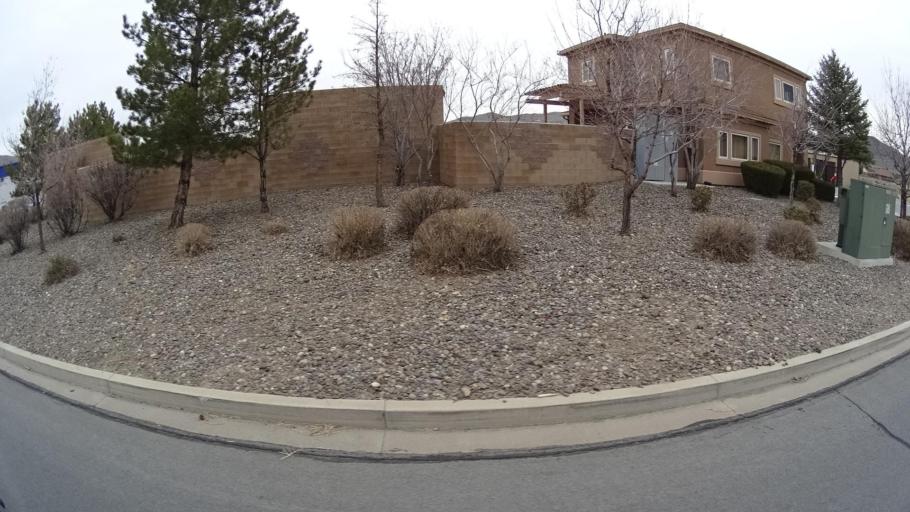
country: US
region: Nevada
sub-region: Washoe County
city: Spanish Springs
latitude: 39.6779
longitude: -119.7031
